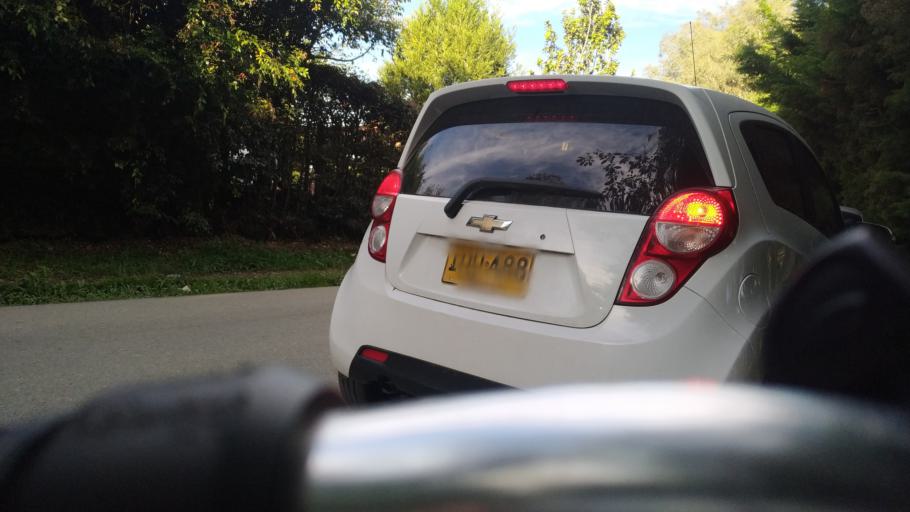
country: CO
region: Antioquia
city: Rionegro
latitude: 6.1328
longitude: -75.3858
